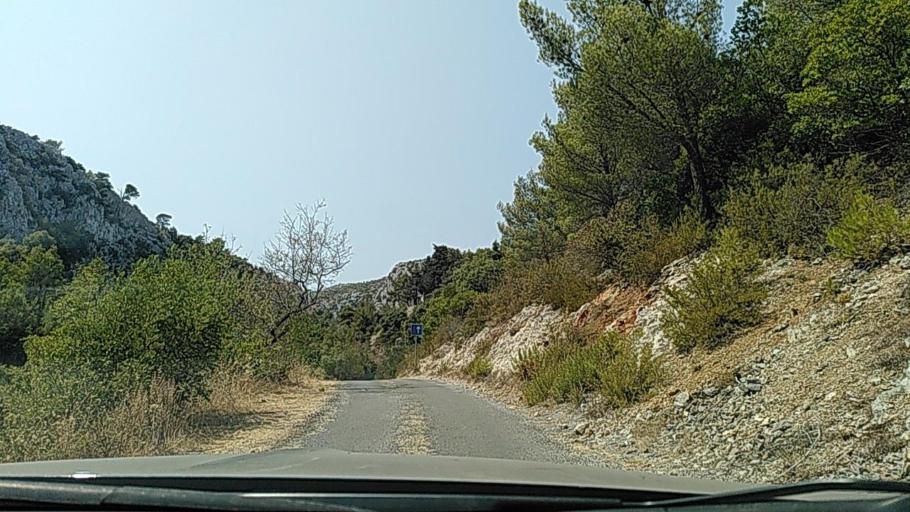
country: HR
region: Splitsko-Dalmatinska
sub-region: Grad Hvar
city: Hvar
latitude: 43.1672
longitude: 16.5072
